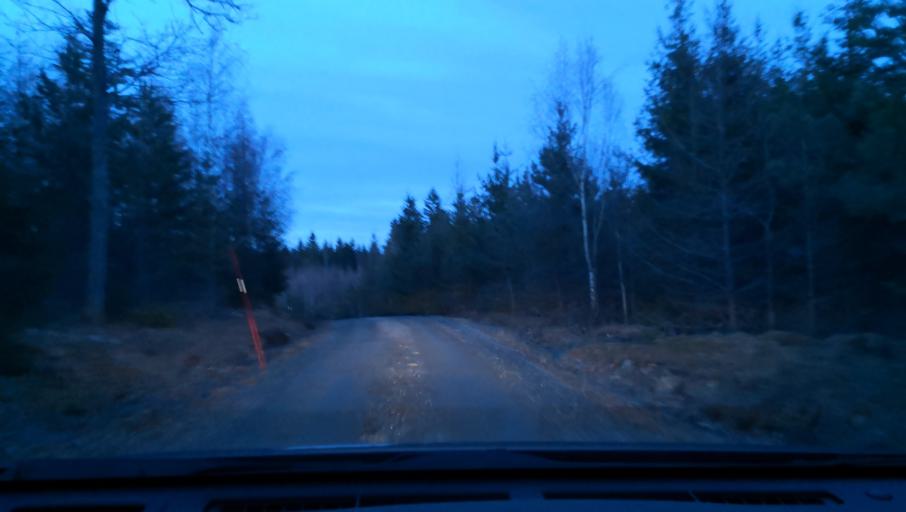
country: SE
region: Uppsala
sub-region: Enkopings Kommun
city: Dalby
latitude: 59.5627
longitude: 17.3727
